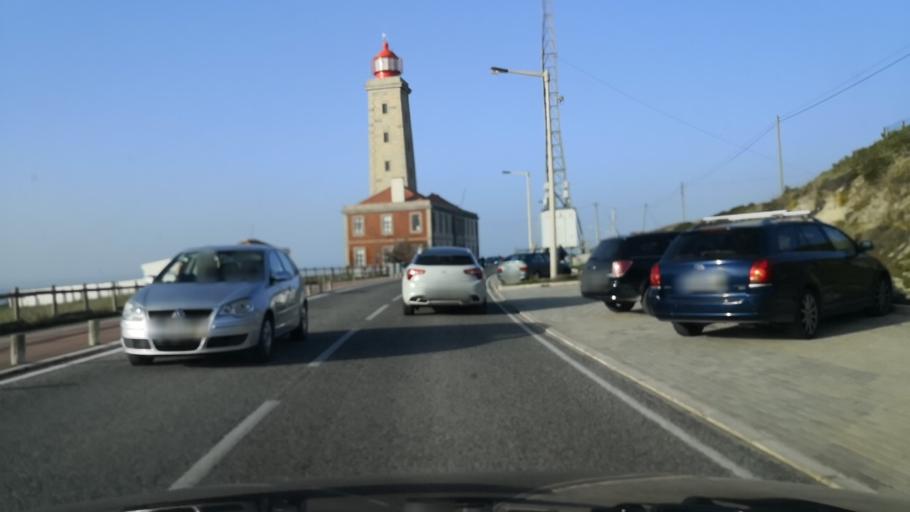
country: PT
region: Leiria
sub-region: Alcobaca
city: Pataias
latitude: 39.7631
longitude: -9.0309
